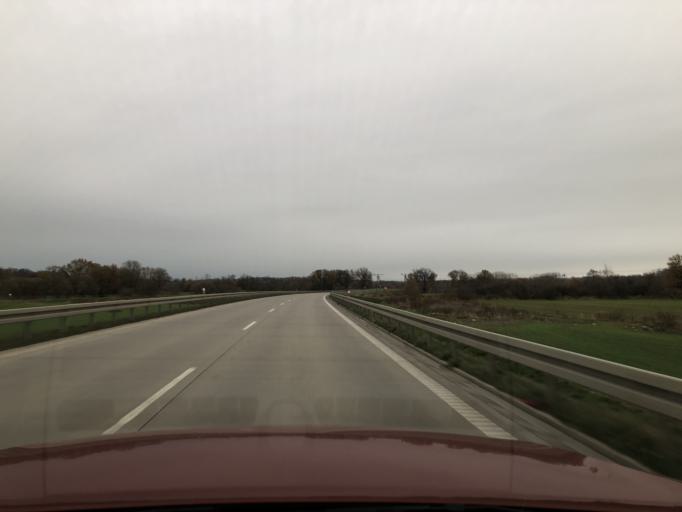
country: PL
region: Lower Silesian Voivodeship
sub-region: Powiat swidnicki
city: Zarow
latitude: 50.9490
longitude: 16.4829
